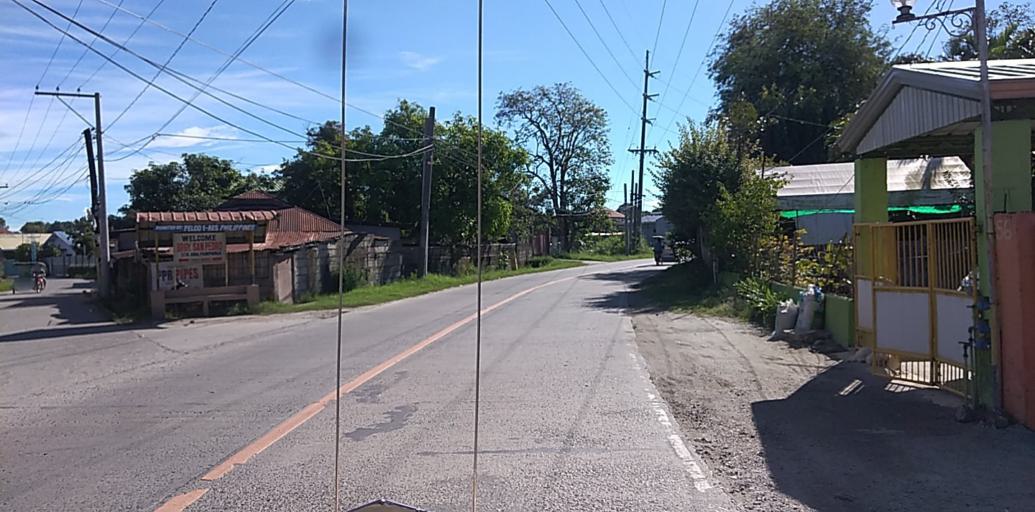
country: PH
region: Central Luzon
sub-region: Province of Pampanga
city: Santo Domingo
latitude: 15.0722
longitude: 120.7614
